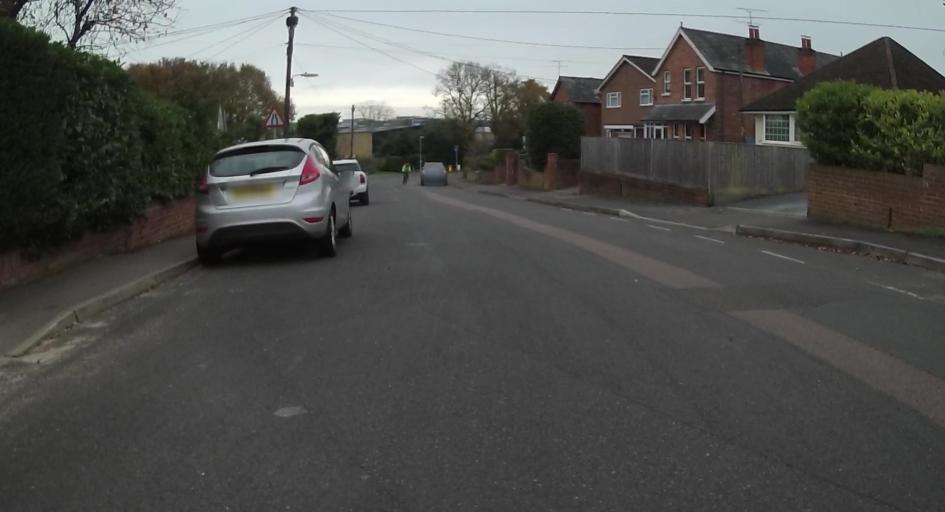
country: GB
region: England
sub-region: Hampshire
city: Farnborough
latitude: 51.2908
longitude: -0.7651
